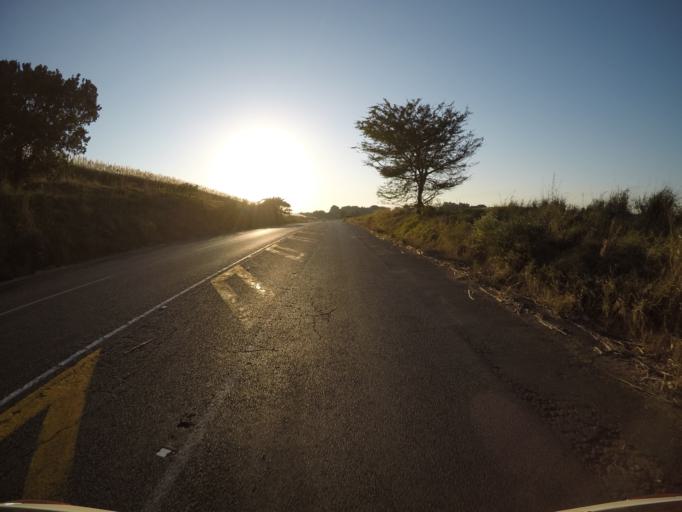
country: ZA
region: KwaZulu-Natal
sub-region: uThungulu District Municipality
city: Eshowe
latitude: -28.9495
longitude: 31.6745
